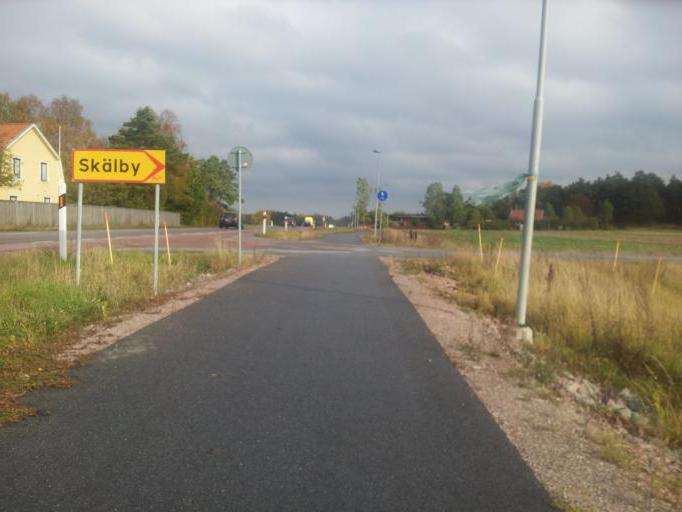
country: SE
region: Uppsala
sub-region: Uppsala Kommun
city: Gamla Uppsala
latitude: 59.8921
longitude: 17.7011
